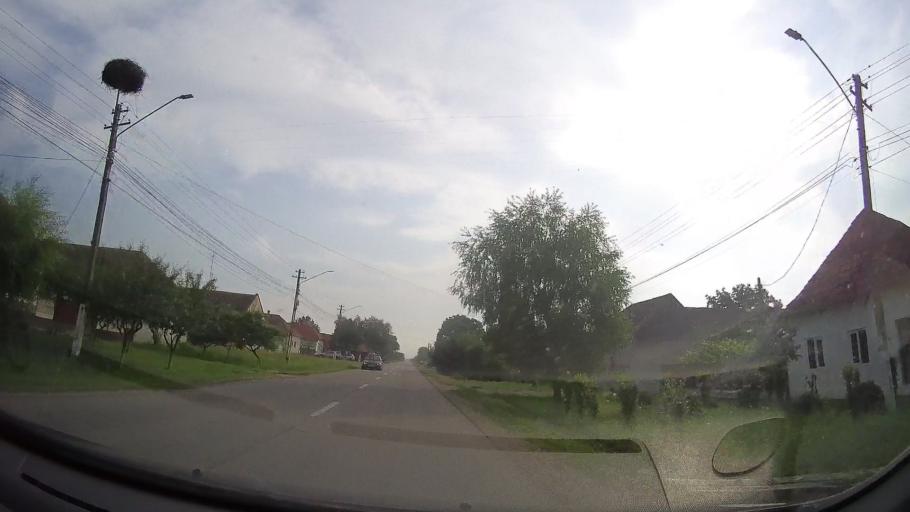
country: RO
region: Timis
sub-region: Comuna Peciu Nou
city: Peciu Nou
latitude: 45.6070
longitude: 21.0601
